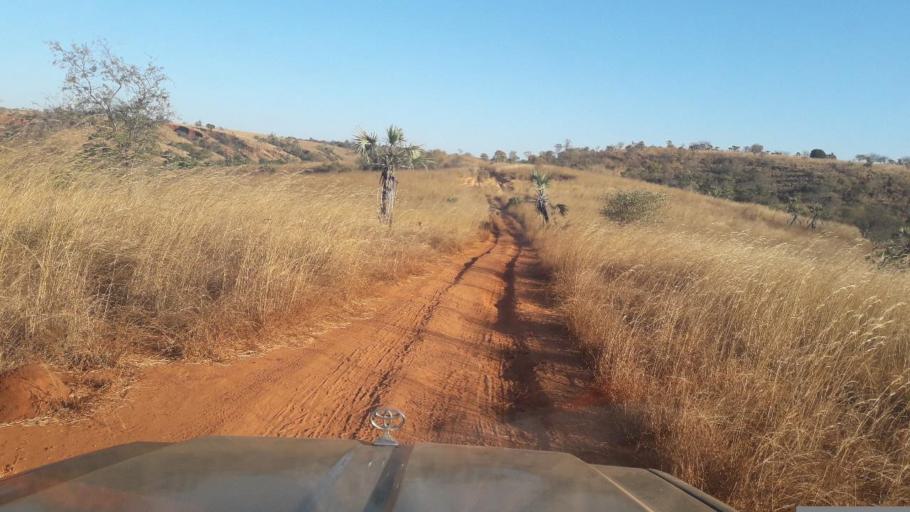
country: MG
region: Boeny
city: Sitampiky
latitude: -16.4937
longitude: 45.6075
